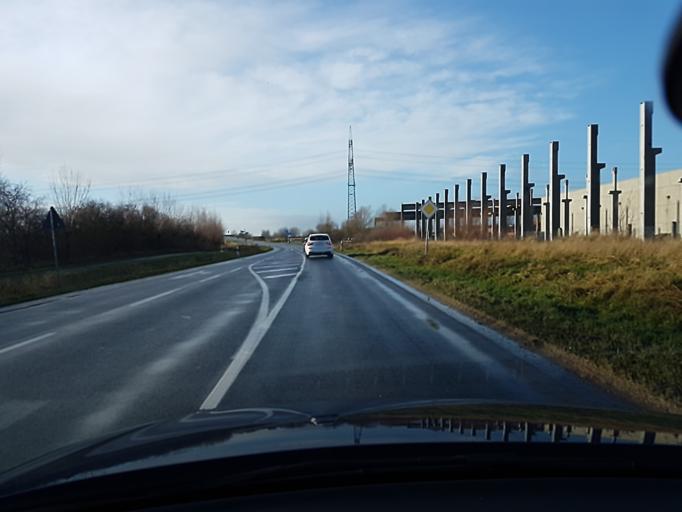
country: DE
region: Mecklenburg-Vorpommern
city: Kavelstorf
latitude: 54.0120
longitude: 12.2086
